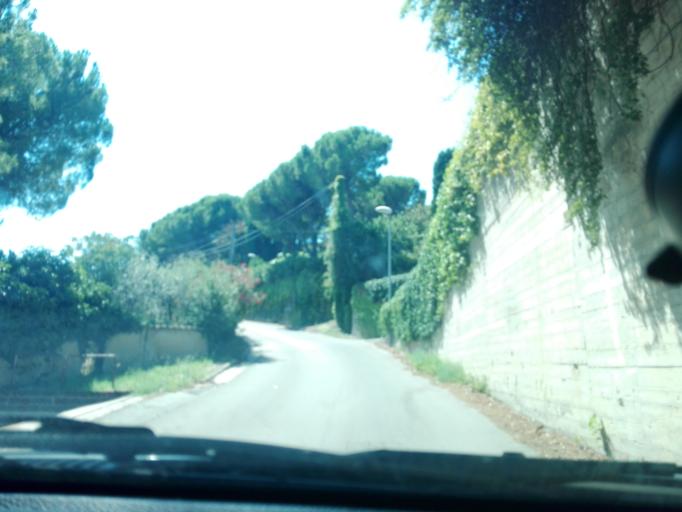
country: IT
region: Abruzzo
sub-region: Provincia di Pescara
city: Montesilvano Marina
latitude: 42.4972
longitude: 14.1589
